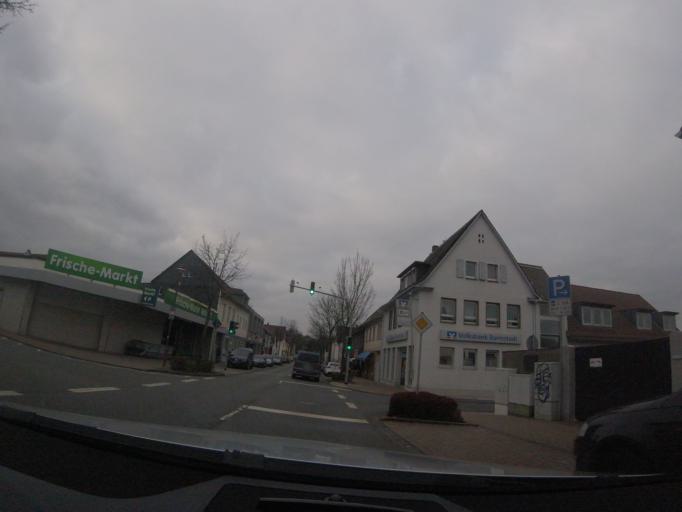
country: DE
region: Hesse
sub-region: Regierungsbezirk Darmstadt
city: Rossdorf
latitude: 49.8590
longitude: 8.7550
